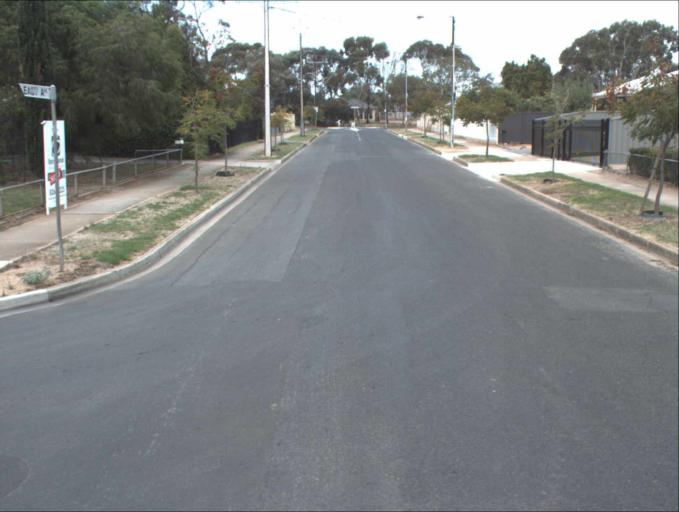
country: AU
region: South Australia
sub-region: Port Adelaide Enfield
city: Enfield
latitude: -34.8516
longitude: 138.6216
